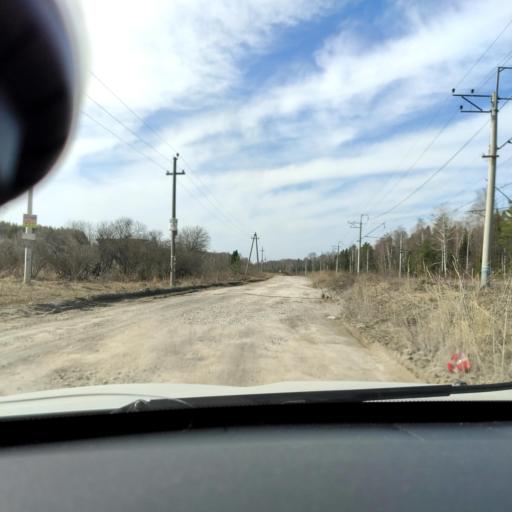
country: RU
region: Perm
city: Overyata
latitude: 58.0567
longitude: 55.9930
